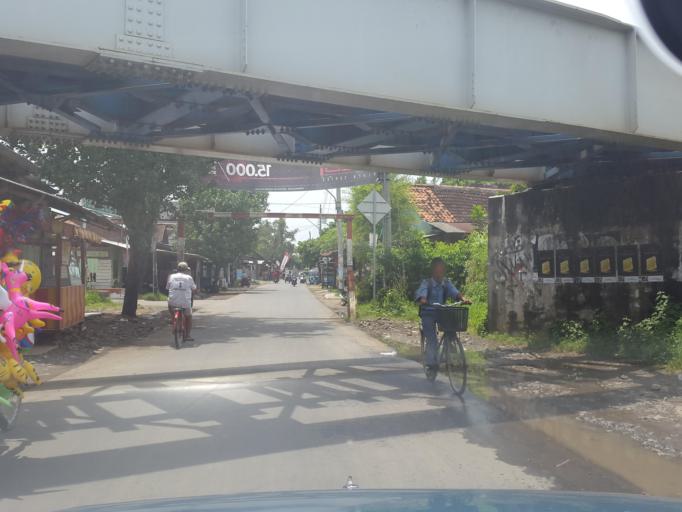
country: ID
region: Central Java
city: Wiradesa
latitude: -6.8912
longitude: 109.6378
